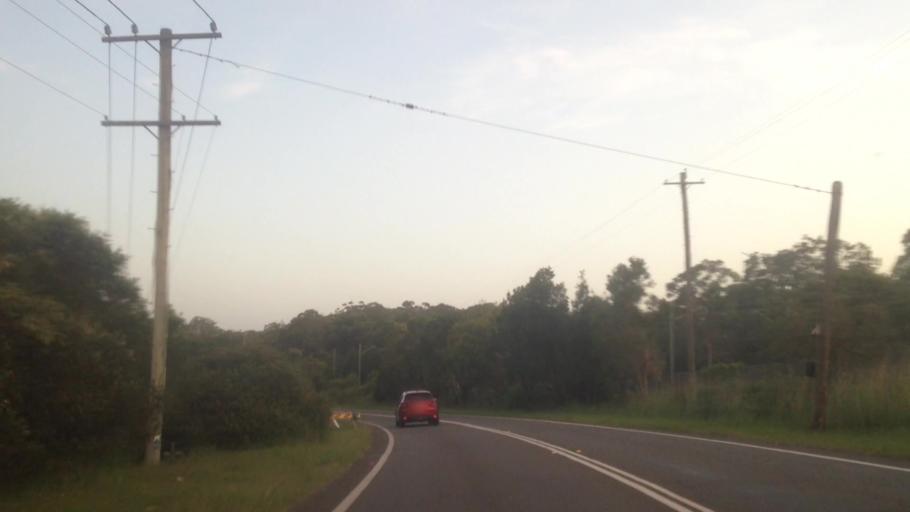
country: AU
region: New South Wales
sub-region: Lake Macquarie Shire
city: Dora Creek
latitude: -33.0968
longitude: 151.4975
